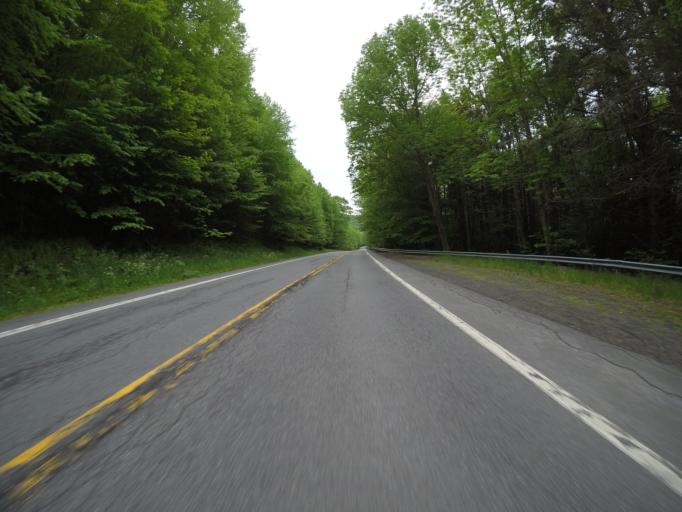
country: US
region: New York
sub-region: Sullivan County
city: Livingston Manor
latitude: 42.0743
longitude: -74.8721
